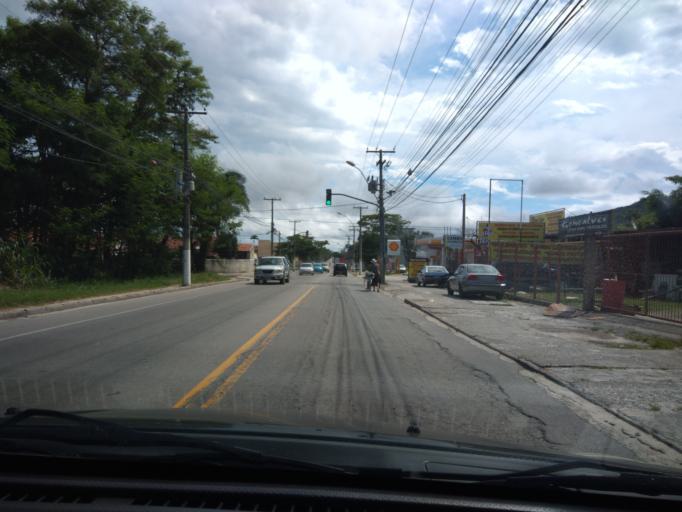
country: BR
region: Rio de Janeiro
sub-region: Niteroi
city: Niteroi
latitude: -22.9307
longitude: -43.0167
